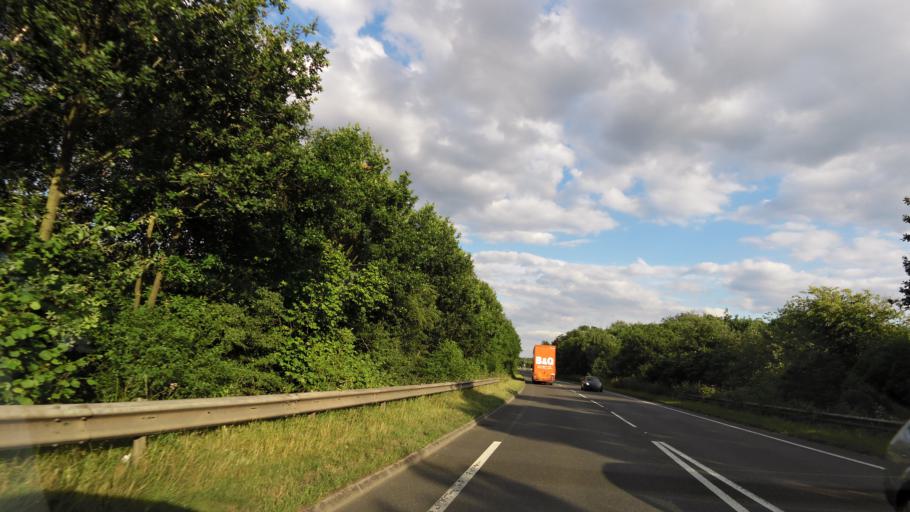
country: GB
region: England
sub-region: Nottinghamshire
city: Worksop
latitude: 53.3138
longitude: -1.1492
